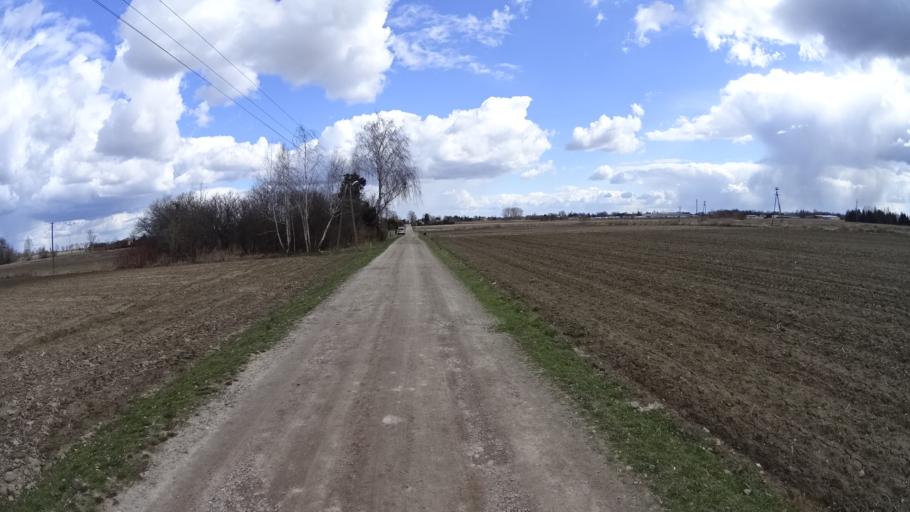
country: PL
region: Masovian Voivodeship
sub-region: Powiat warszawski zachodni
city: Jozefow
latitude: 52.2200
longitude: 20.6788
